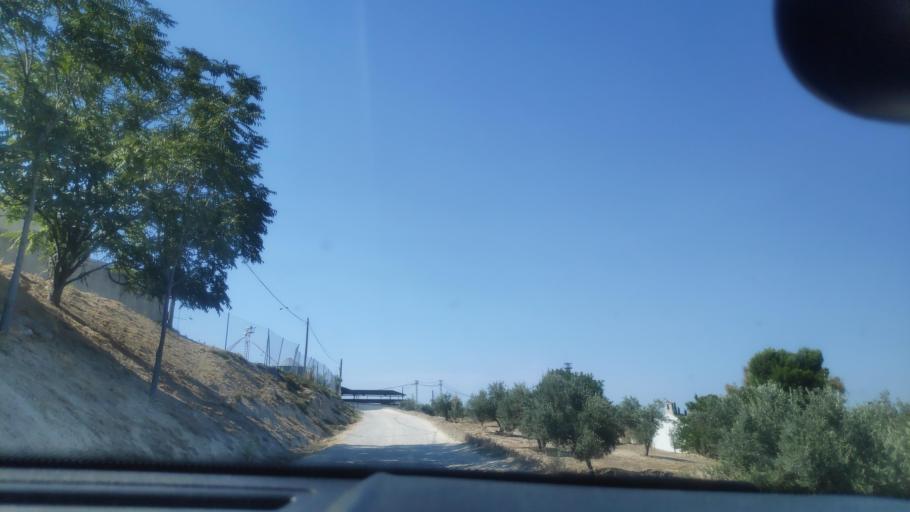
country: ES
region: Andalusia
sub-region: Provincia de Jaen
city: Jaen
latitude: 37.8249
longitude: -3.7592
